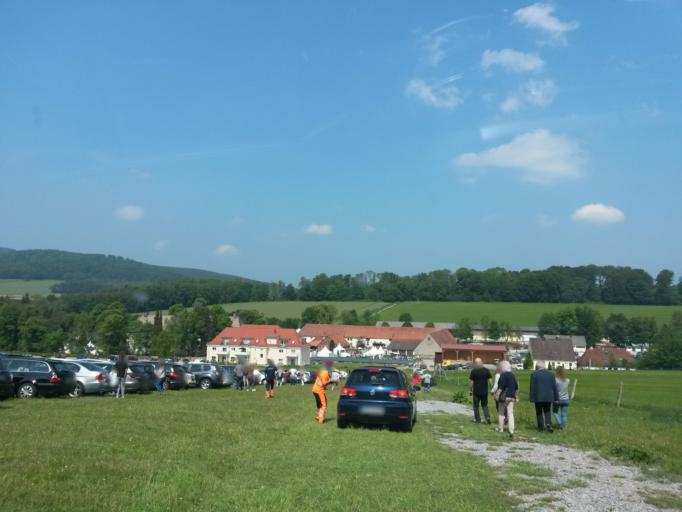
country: DE
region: North Rhine-Westphalia
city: Balve
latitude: 51.3397
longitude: 7.8903
